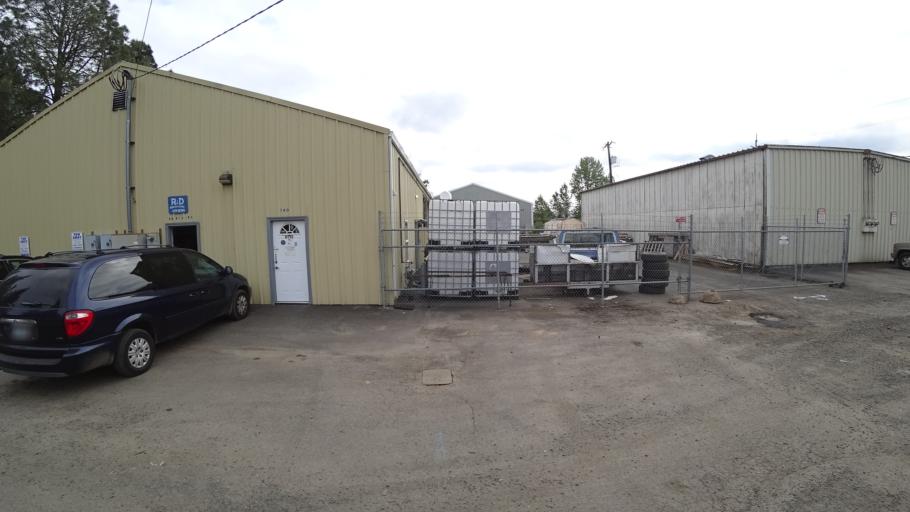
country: US
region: Oregon
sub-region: Washington County
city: Hillsboro
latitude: 45.5220
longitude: -122.9981
